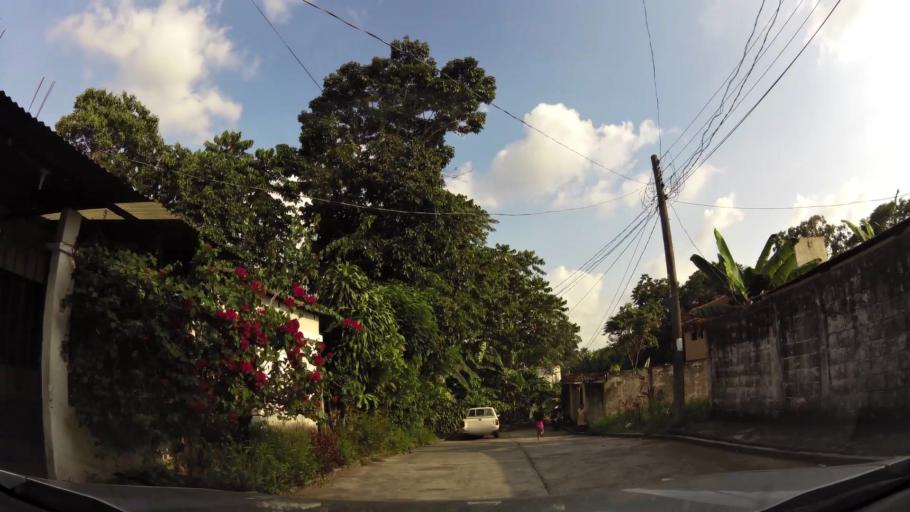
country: GT
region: Retalhuleu
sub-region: Municipio de Retalhuleu
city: Retalhuleu
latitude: 14.5448
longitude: -91.6725
